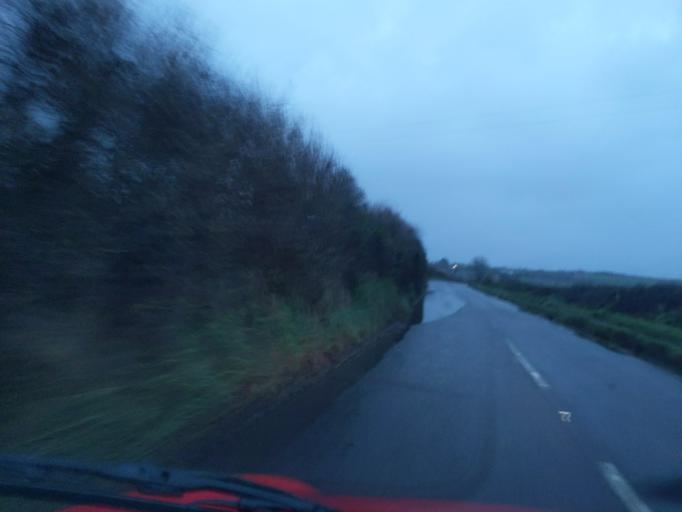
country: GB
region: England
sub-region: Cornwall
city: Saltash
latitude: 50.3629
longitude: -4.2648
